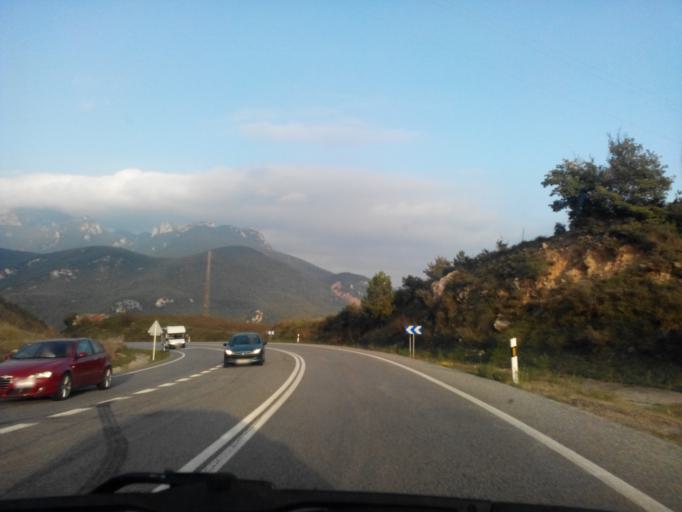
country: ES
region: Catalonia
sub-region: Provincia de Barcelona
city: Berga
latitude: 42.1276
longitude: 1.8634
